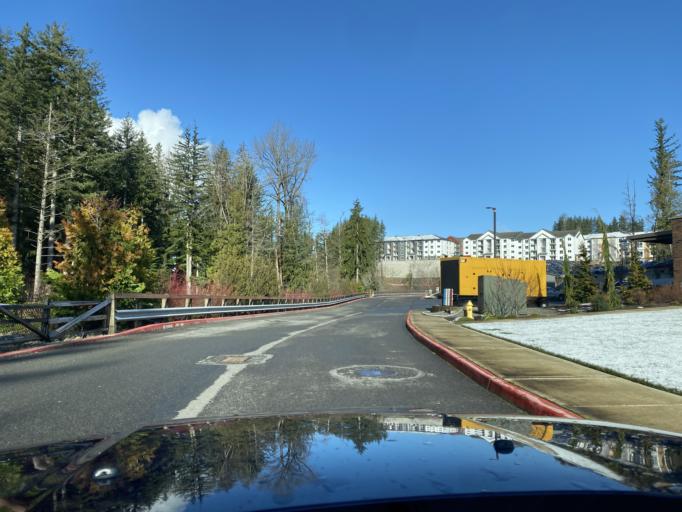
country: US
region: Washington
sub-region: King County
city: Fall City
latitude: 47.5125
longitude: -121.8865
